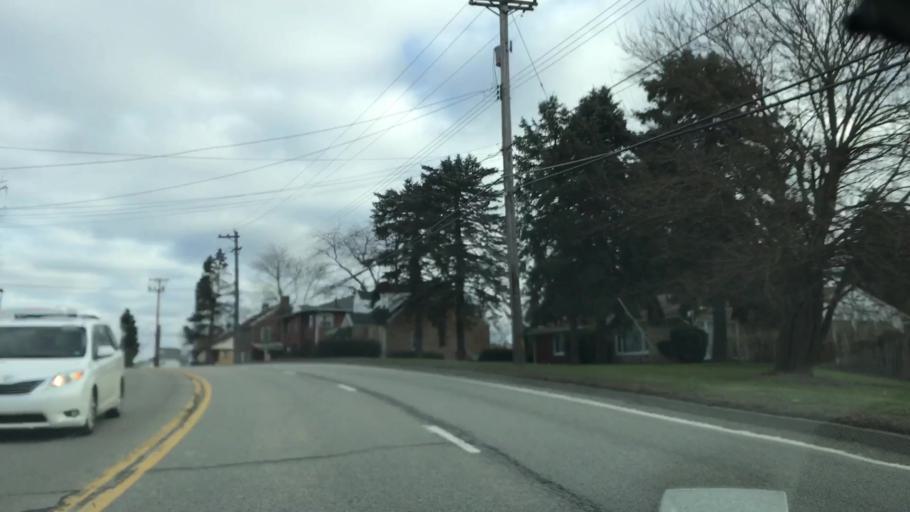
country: US
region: Pennsylvania
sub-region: Beaver County
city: Aliquippa
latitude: 40.6026
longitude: -80.2903
